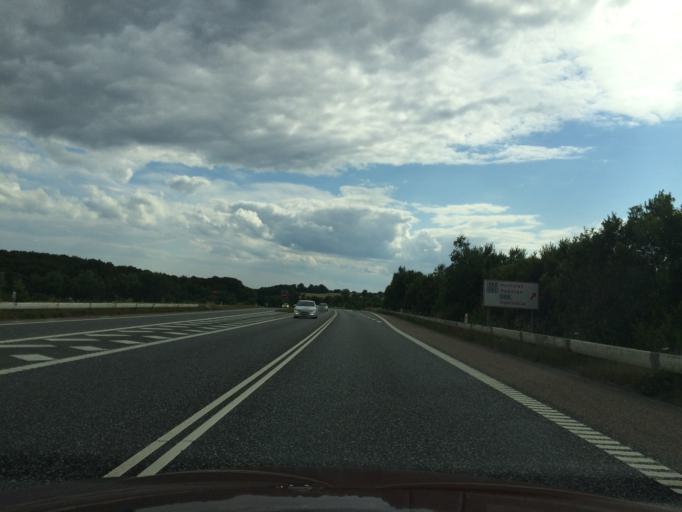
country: DK
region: Central Jutland
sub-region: Syddjurs Kommune
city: Hornslet
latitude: 56.2941
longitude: 10.3354
